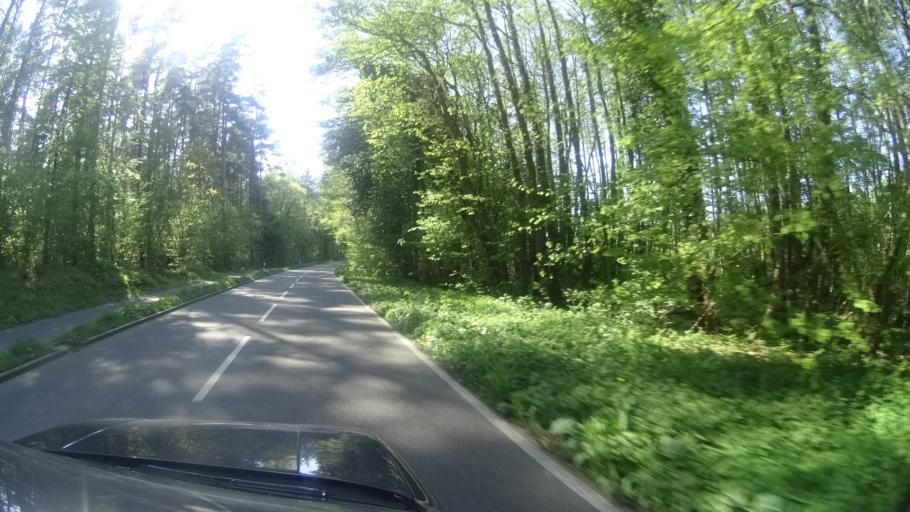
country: DE
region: Mecklenburg-Vorpommern
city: Ostseebad Dierhagen
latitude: 54.2724
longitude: 12.3343
